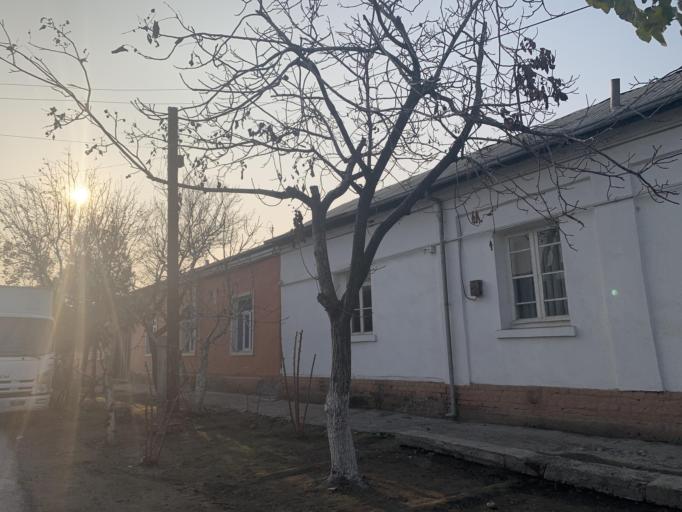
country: UZ
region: Fergana
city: Qo`qon
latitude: 40.5414
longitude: 70.9262
